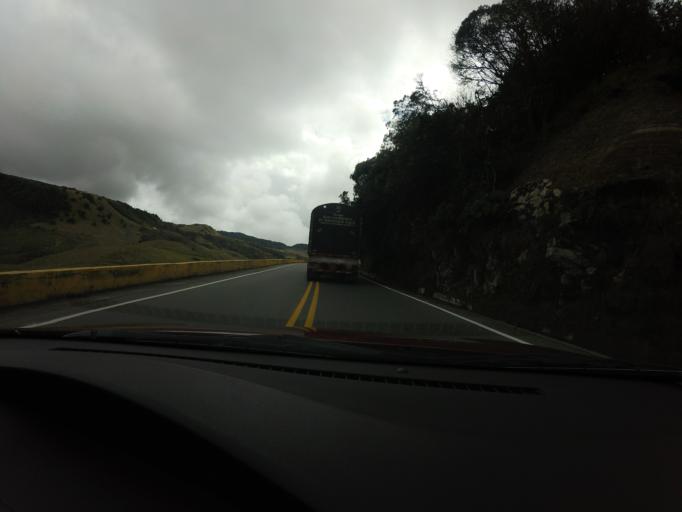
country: CO
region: Tolima
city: Herveo
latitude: 5.0559
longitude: -75.3198
